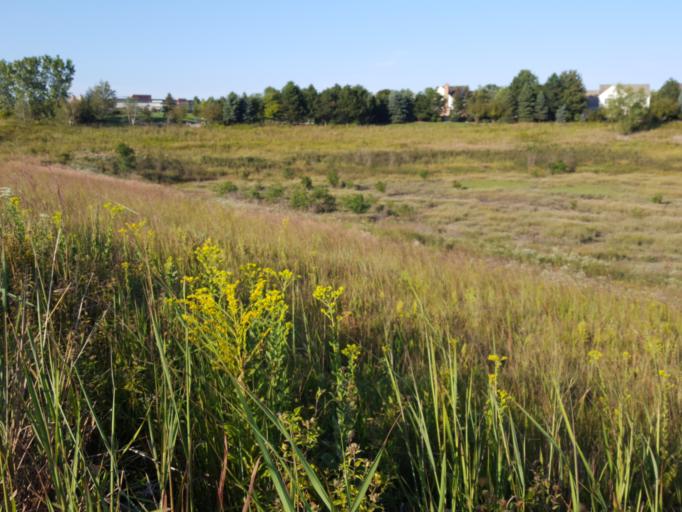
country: US
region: Illinois
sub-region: Cook County
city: Northfield
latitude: 42.1021
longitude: -87.8095
